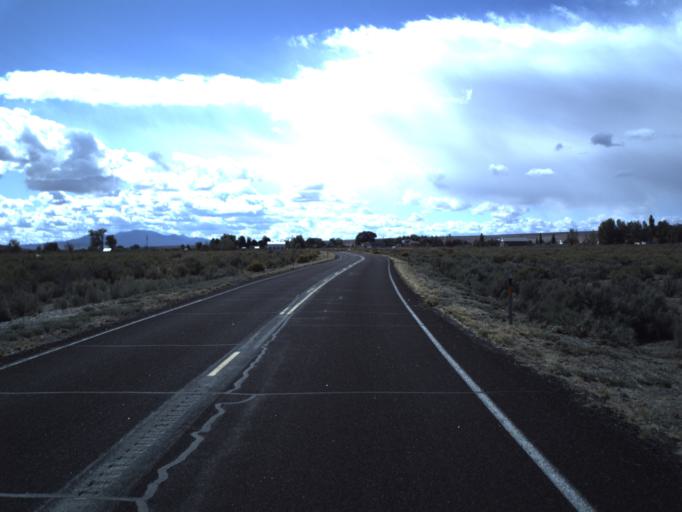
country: US
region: Nevada
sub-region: White Pine County
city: McGill
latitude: 38.9456
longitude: -114.0331
